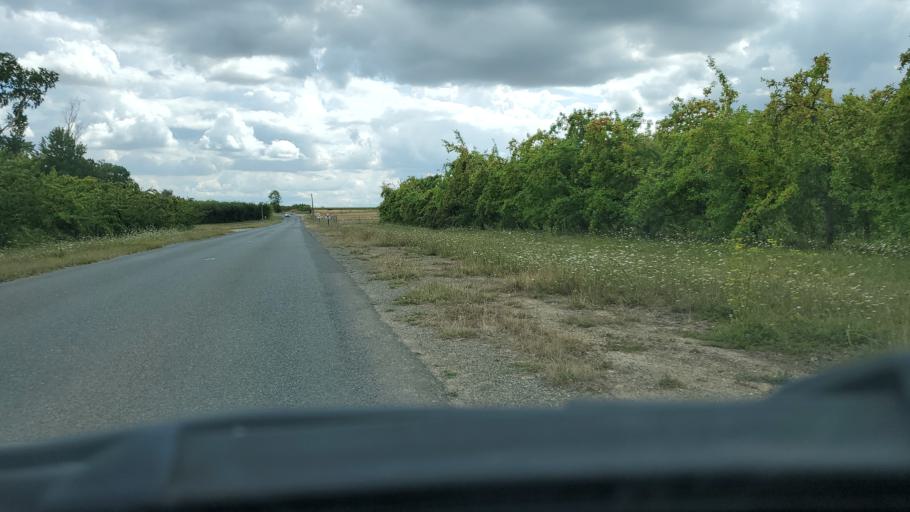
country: FR
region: Ile-de-France
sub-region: Departement de Seine-et-Marne
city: Pommeuse
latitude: 48.8461
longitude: 3.0189
